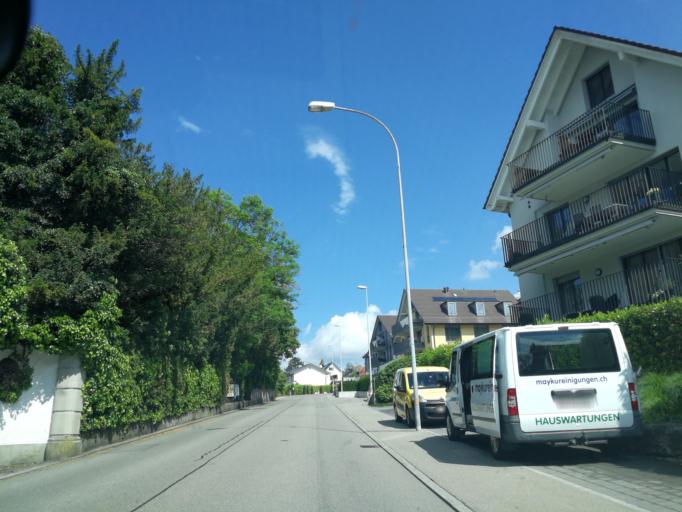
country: CH
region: Zurich
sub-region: Bezirk Meilen
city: Erlenbach
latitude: 47.3062
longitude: 8.5975
